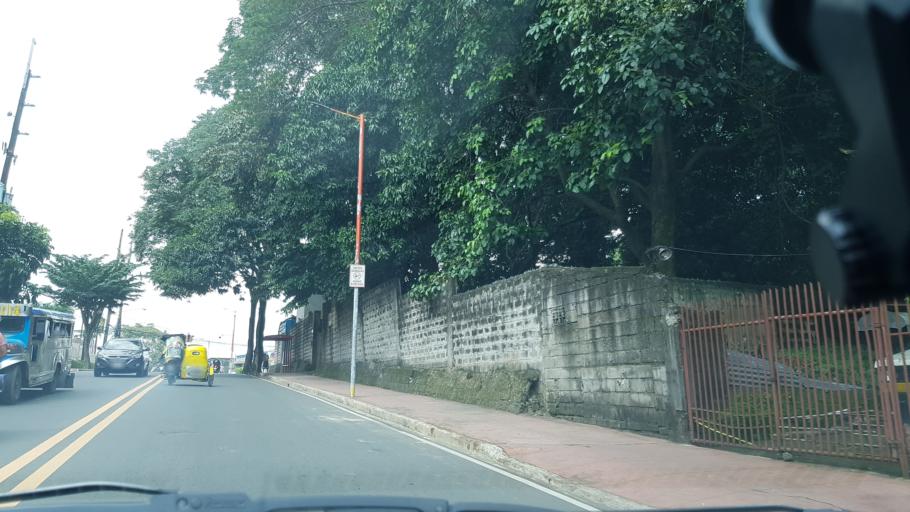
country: PH
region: Calabarzon
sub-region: Province of Rizal
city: Antipolo
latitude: 14.6593
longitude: 121.1186
